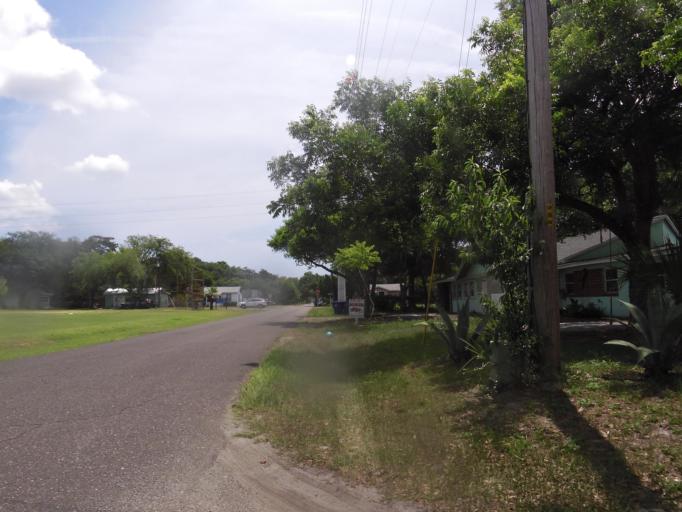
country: US
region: Florida
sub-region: Nassau County
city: Fernandina Beach
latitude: 30.6617
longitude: -81.4585
